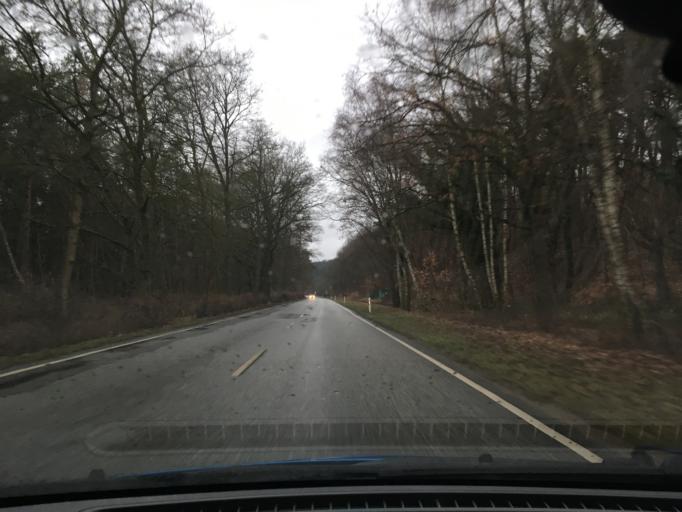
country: DE
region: Lower Saxony
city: Tespe
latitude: 53.4137
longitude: 10.4011
